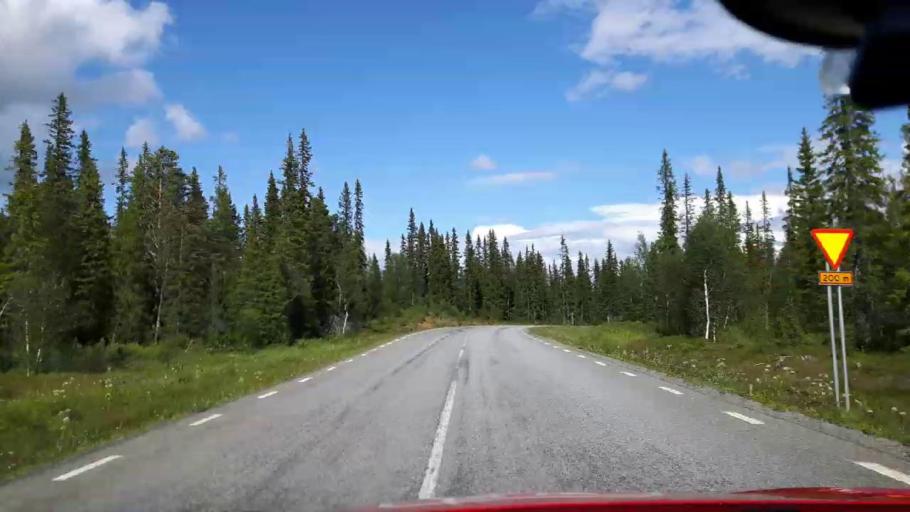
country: SE
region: Jaemtland
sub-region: Are Kommun
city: Are
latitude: 63.2285
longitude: 13.1561
